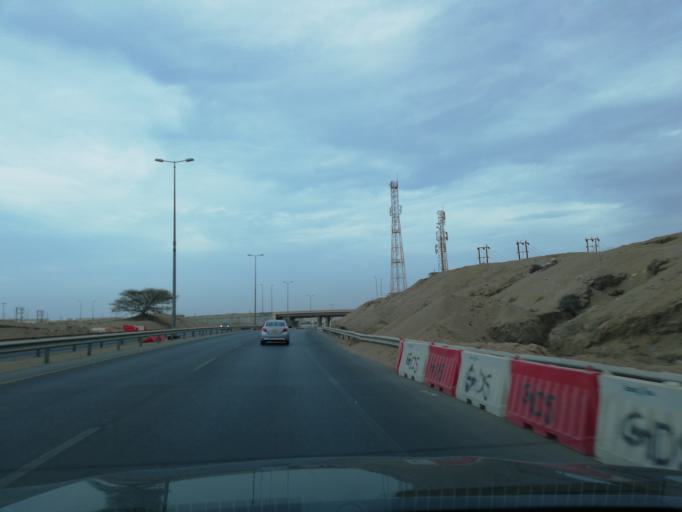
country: OM
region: Muhafazat Masqat
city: Bawshar
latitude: 23.5798
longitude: 58.4146
